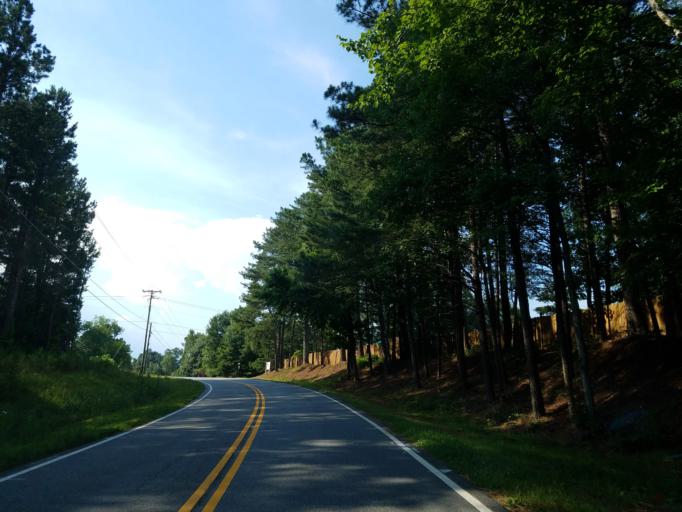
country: US
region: Georgia
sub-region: Forsyth County
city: Cumming
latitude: 34.2906
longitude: -84.0666
